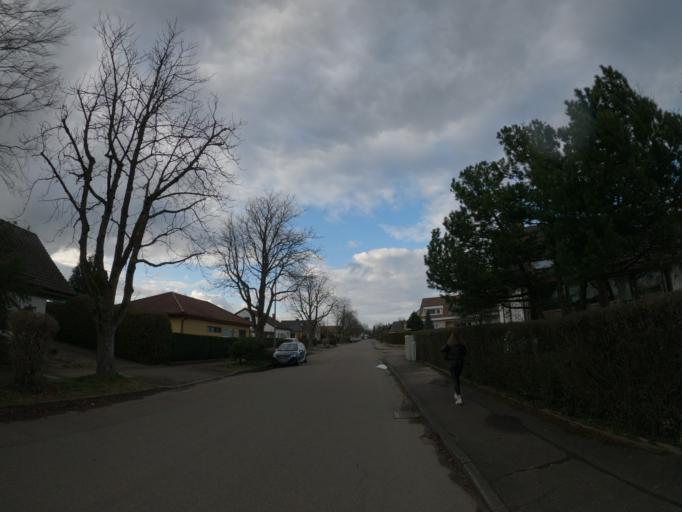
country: DE
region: Baden-Wuerttemberg
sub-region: Regierungsbezirk Stuttgart
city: Heiningen
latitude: 48.6584
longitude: 9.6401
